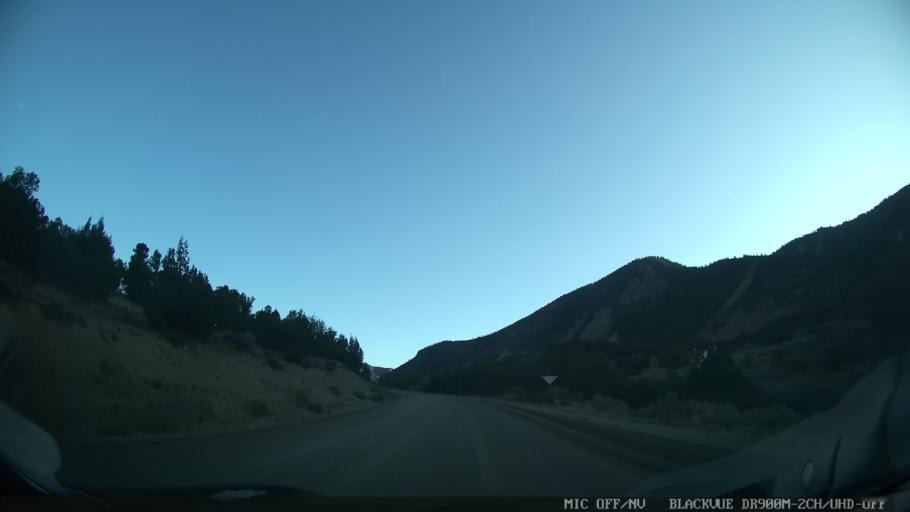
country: US
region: Colorado
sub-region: Grand County
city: Kremmling
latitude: 39.9801
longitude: -106.4975
